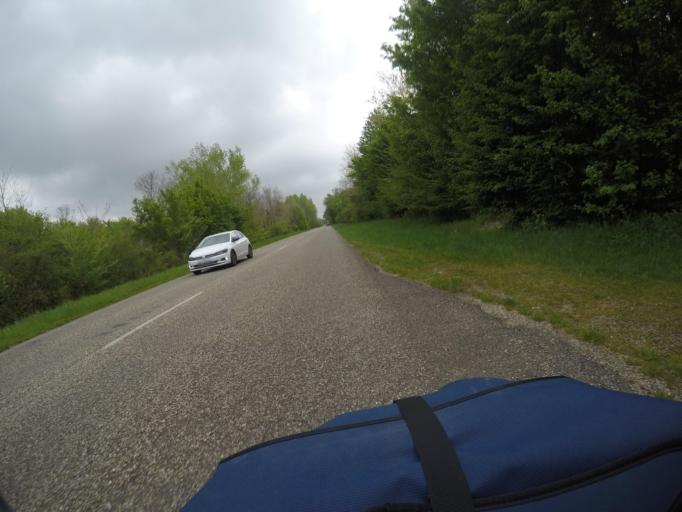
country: FR
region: Alsace
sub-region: Departement du Bas-Rhin
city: Drusenheim
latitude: 48.7828
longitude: 7.9722
